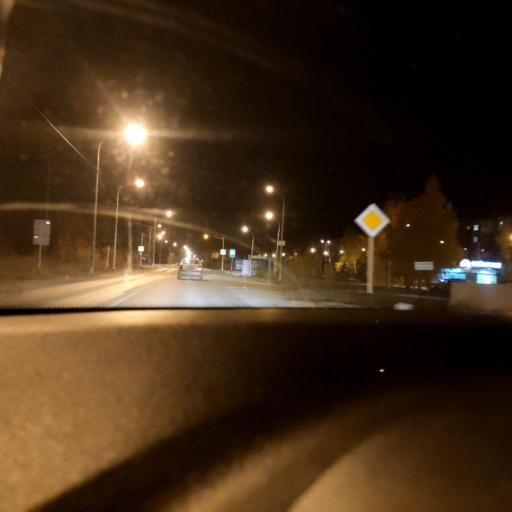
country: RU
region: Samara
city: Smyshlyayevka
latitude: 53.2683
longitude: 50.3868
